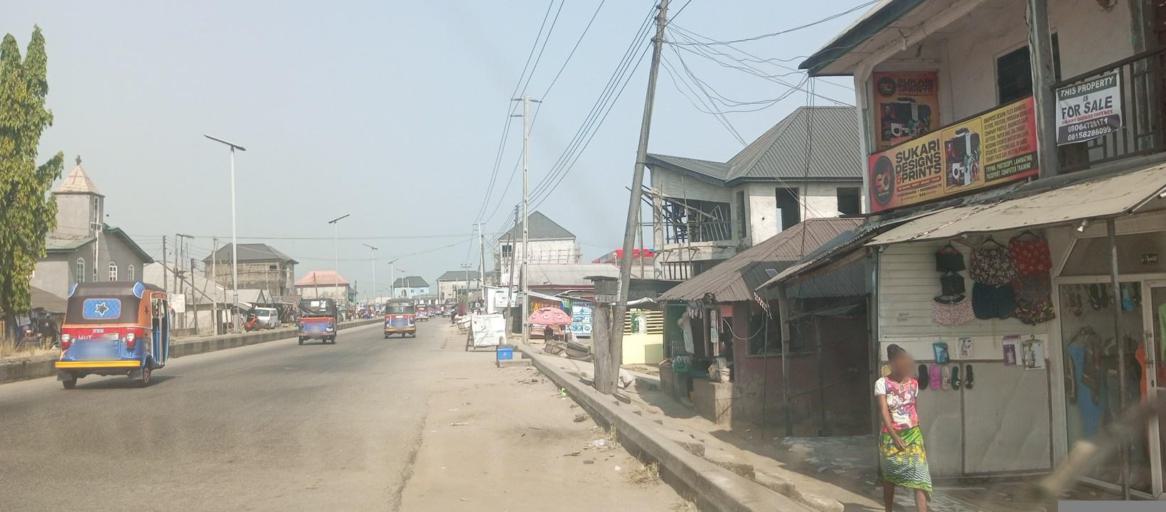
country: NG
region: Bayelsa
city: Yenagoa
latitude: 4.9571
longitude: 6.3626
